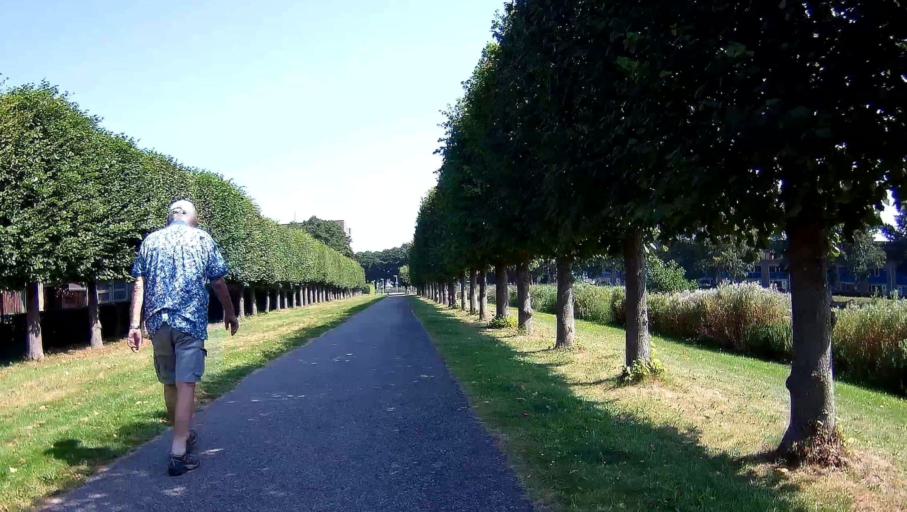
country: NL
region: South Holland
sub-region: Gemeente Zoetermeer
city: Zoetermeer
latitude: 52.0417
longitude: 4.4620
